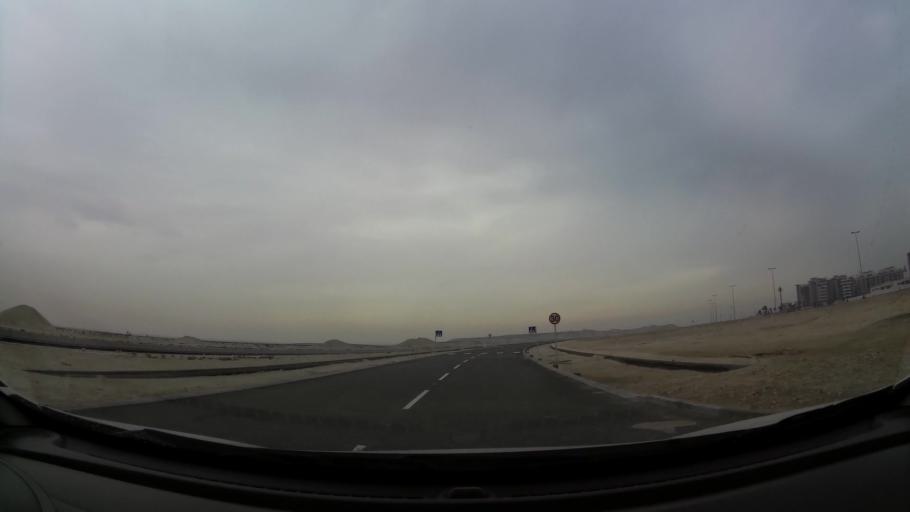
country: BH
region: Central Governorate
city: Dar Kulayb
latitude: 25.8648
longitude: 50.6045
